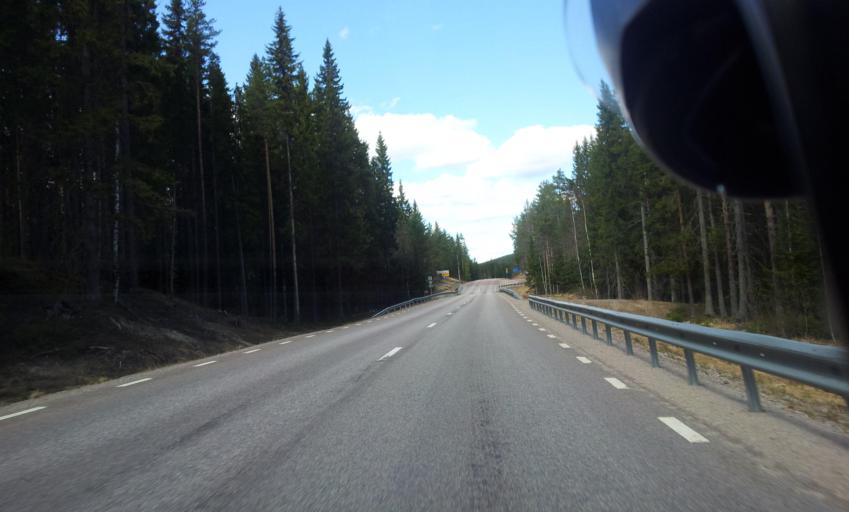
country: SE
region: Gaevleborg
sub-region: Ovanakers Kommun
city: Edsbyn
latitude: 61.1670
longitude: 15.8826
